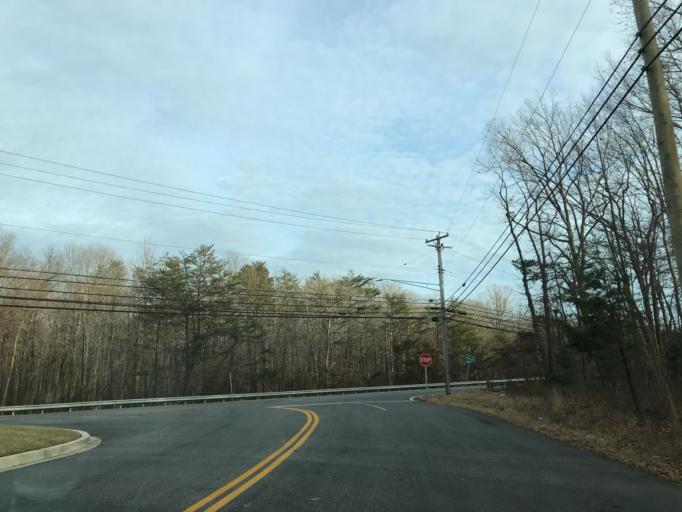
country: US
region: Maryland
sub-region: Harford County
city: Joppatowne
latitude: 39.4505
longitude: -76.3551
